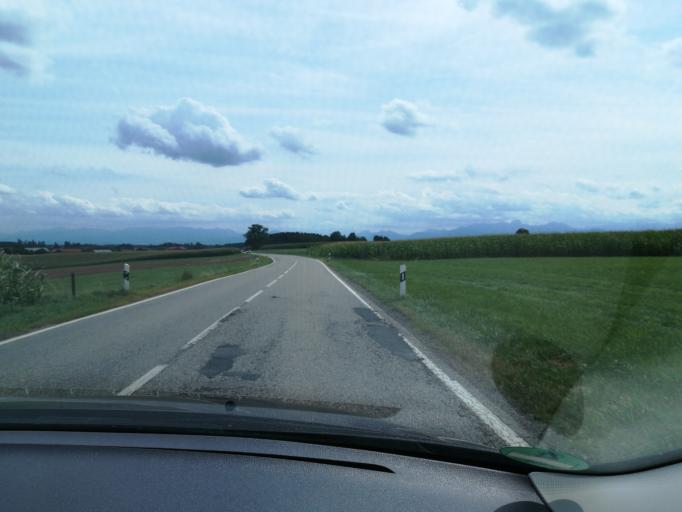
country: DE
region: Bavaria
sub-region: Upper Bavaria
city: Assling
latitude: 47.9634
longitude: 11.9649
